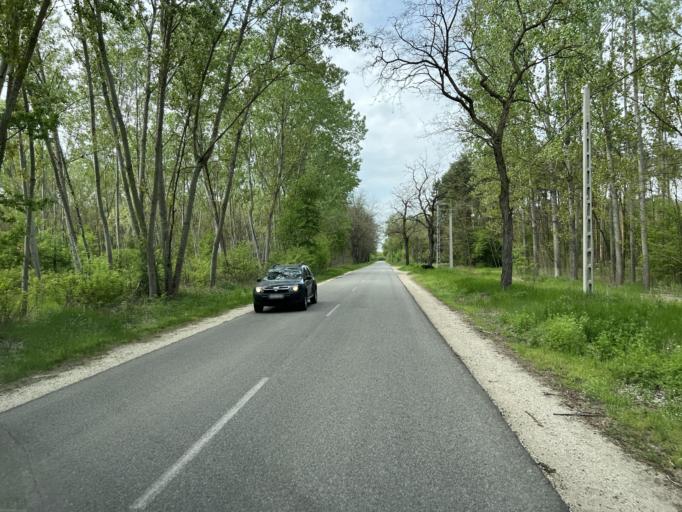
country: HU
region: Pest
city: Csemo
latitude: 47.1390
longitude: 19.6393
